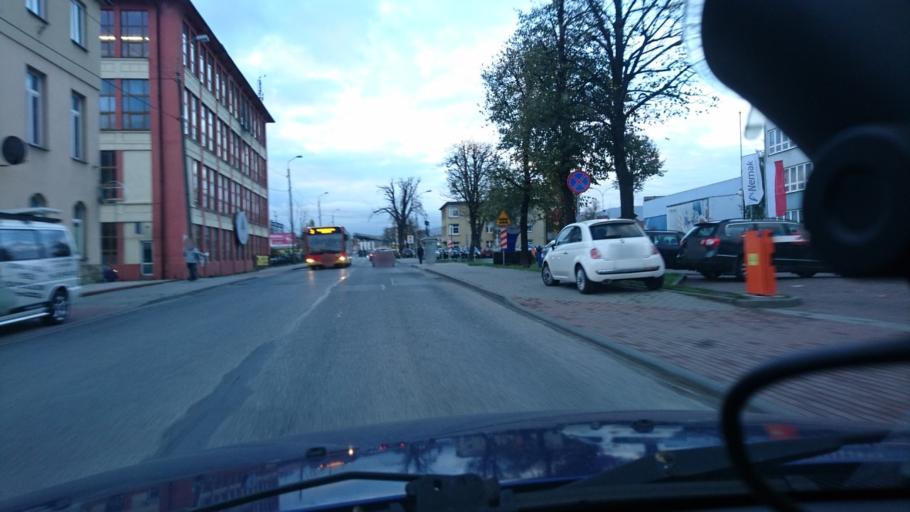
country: PL
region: Silesian Voivodeship
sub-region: Bielsko-Biala
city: Bielsko-Biala
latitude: 49.8363
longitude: 19.0545
